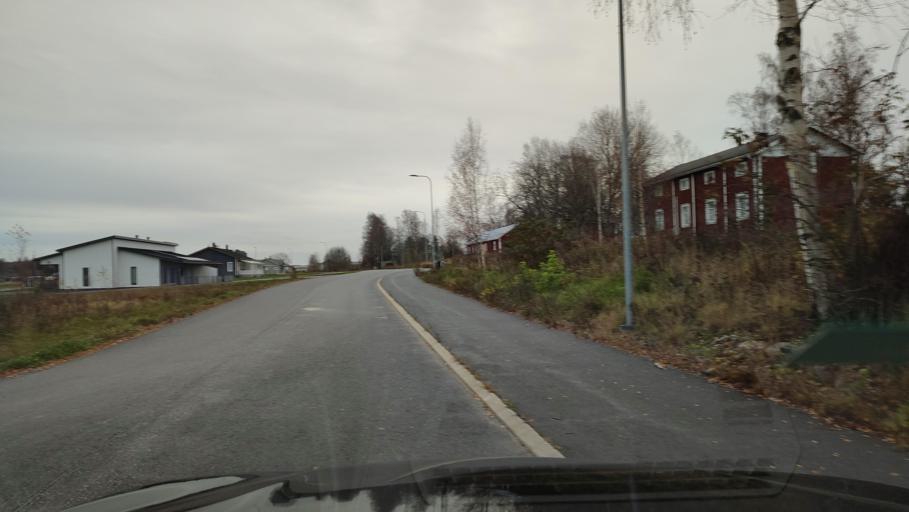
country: FI
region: Ostrobothnia
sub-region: Sydosterbotten
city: Naerpes
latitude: 62.4780
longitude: 21.3248
